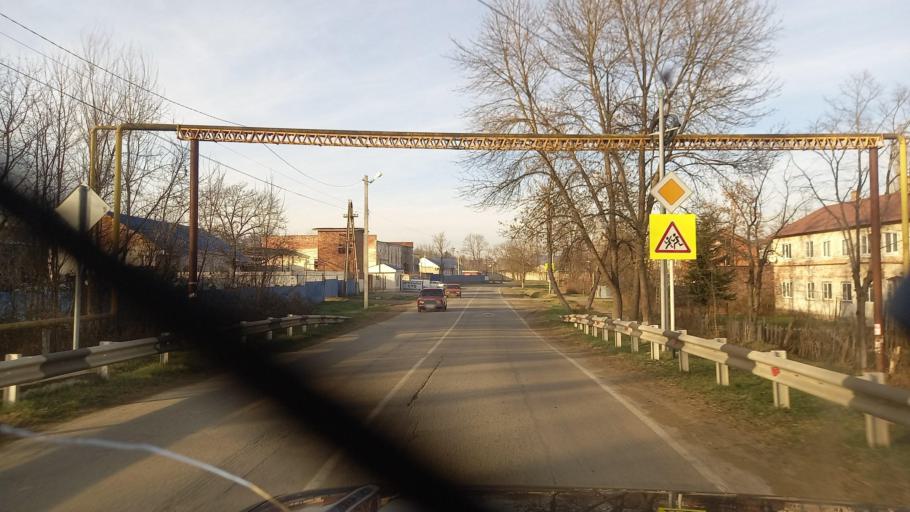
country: RU
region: Krasnodarskiy
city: Khadyzhensk
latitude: 44.4435
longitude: 39.5250
